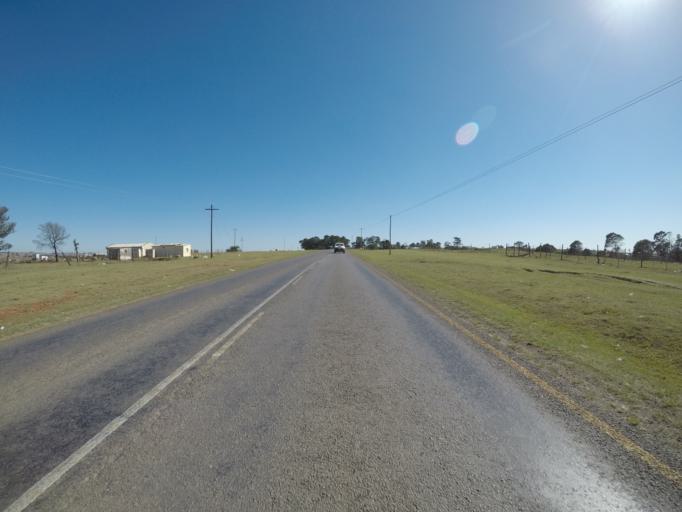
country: ZA
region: Eastern Cape
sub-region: OR Tambo District Municipality
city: Mthatha
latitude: -31.7931
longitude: 28.7451
